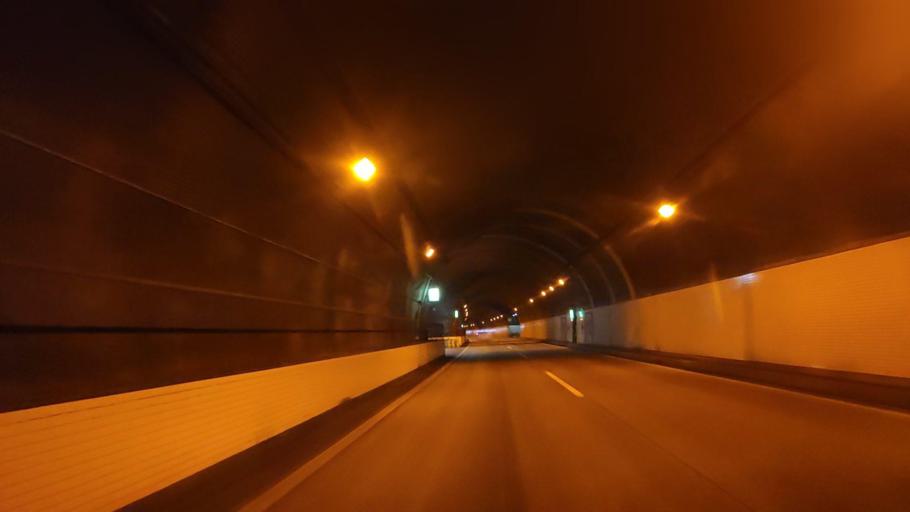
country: JP
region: Toyama
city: Nyuzen
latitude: 36.9720
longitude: 137.6332
